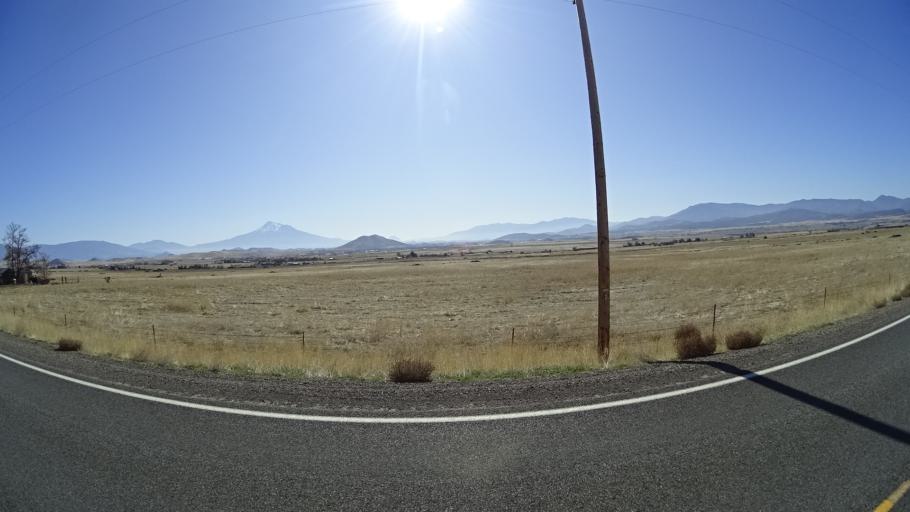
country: US
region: California
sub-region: Siskiyou County
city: Montague
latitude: 41.7699
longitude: -122.5459
